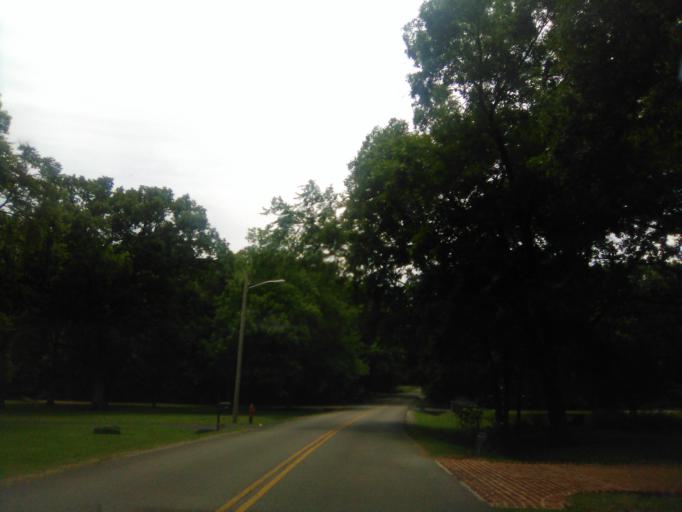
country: US
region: Tennessee
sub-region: Davidson County
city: Belle Meade
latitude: 36.1103
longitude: -86.8764
